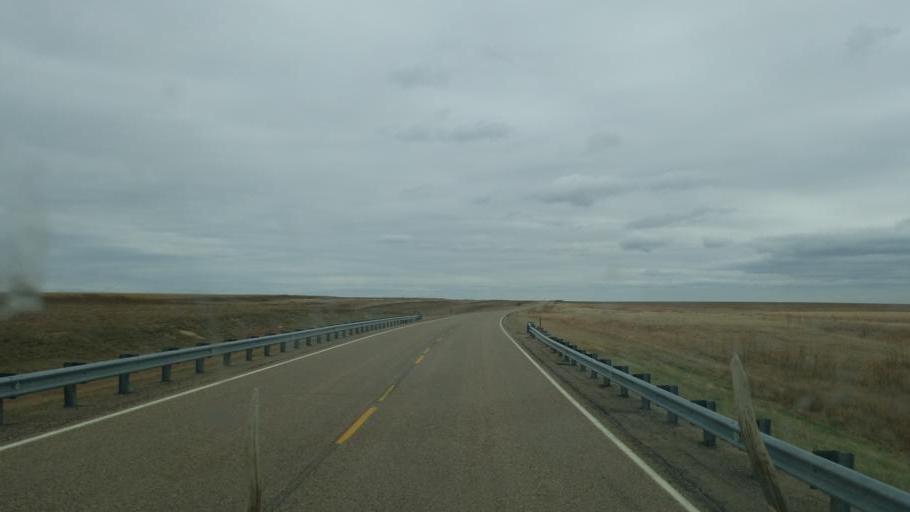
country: US
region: Colorado
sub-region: Cheyenne County
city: Cheyenne Wells
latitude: 38.8487
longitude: -102.1539
